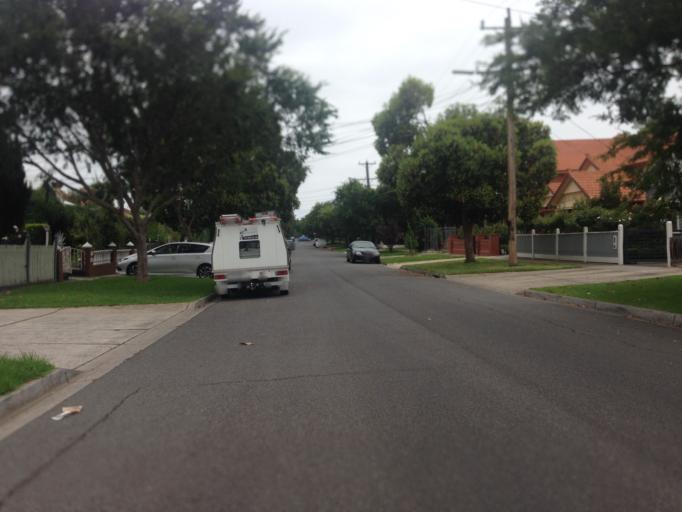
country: AU
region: Victoria
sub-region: Darebin
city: Thornbury
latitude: -37.7633
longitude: 145.0163
